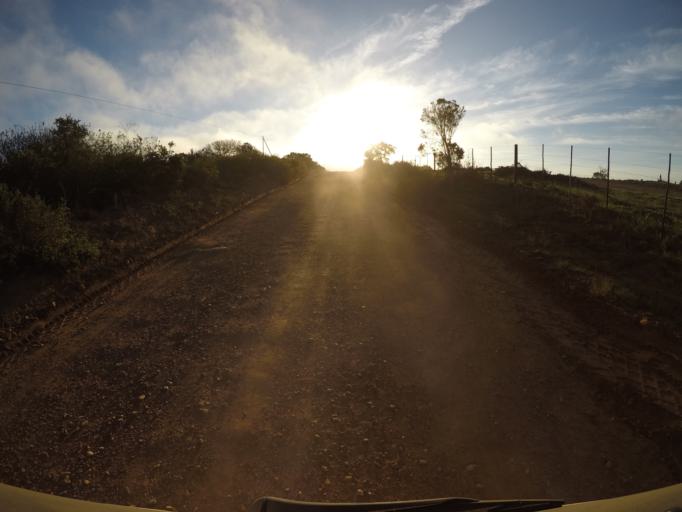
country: ZA
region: Western Cape
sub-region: Eden District Municipality
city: Mossel Bay
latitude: -34.1449
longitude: 22.0174
